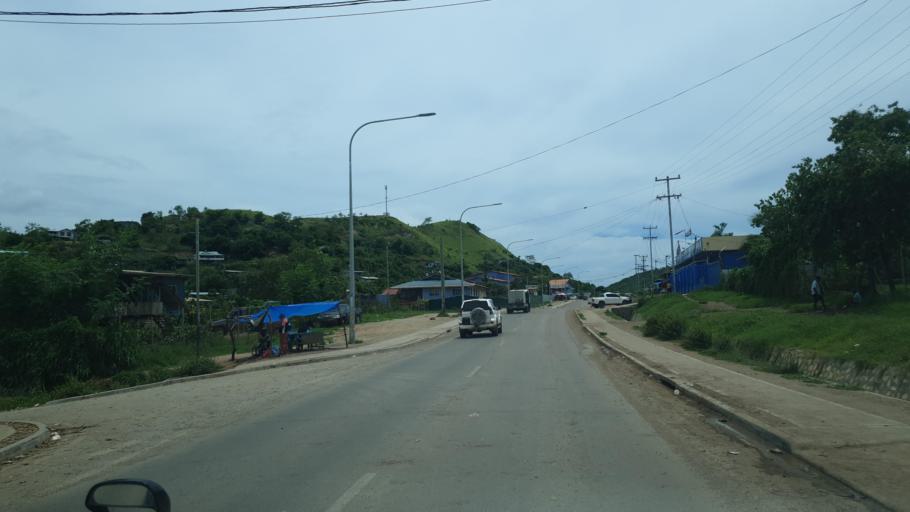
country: PG
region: National Capital
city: Port Moresby
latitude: -9.5183
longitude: 147.2406
